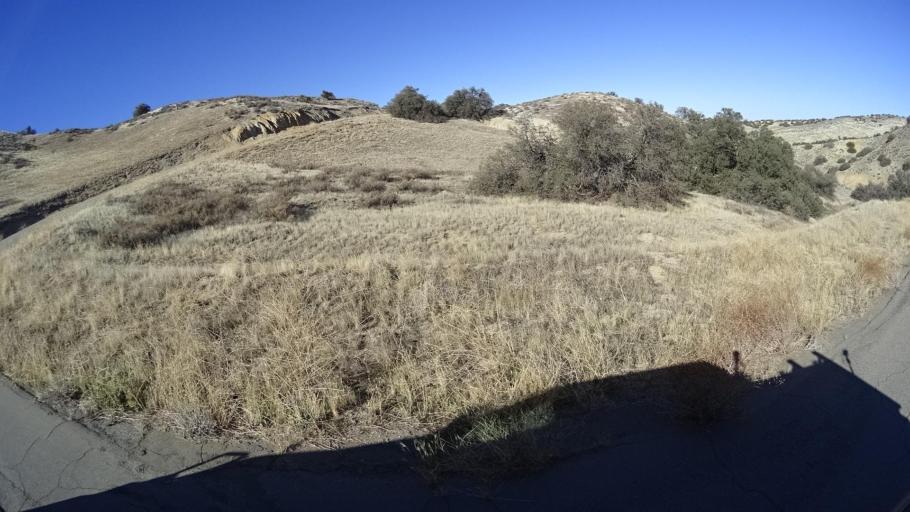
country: US
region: California
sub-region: Kern County
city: Maricopa
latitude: 34.9416
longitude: -119.4024
